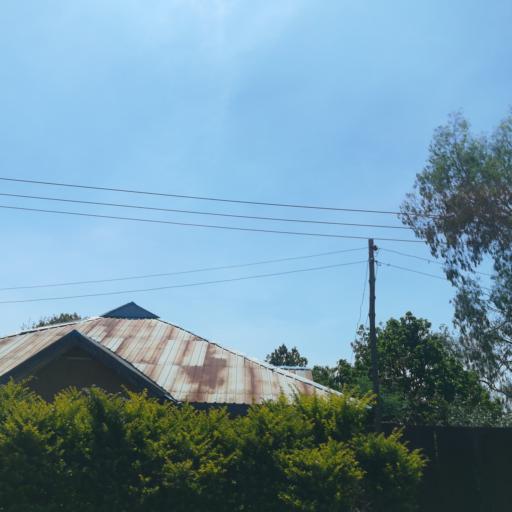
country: NG
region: Plateau
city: Bukuru
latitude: 9.7874
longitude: 8.8769
